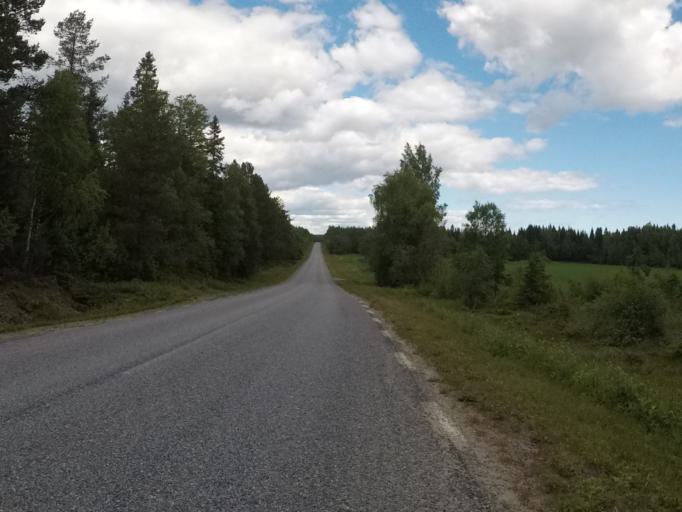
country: SE
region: Vaesterbotten
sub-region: Umea Kommun
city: Saevar
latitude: 63.9398
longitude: 20.7868
